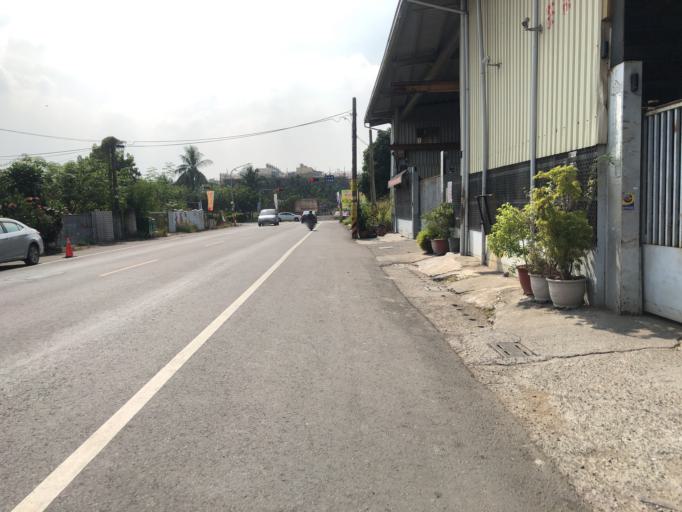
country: TW
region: Taiwan
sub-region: Pingtung
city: Pingtung
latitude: 22.5480
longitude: 120.5339
